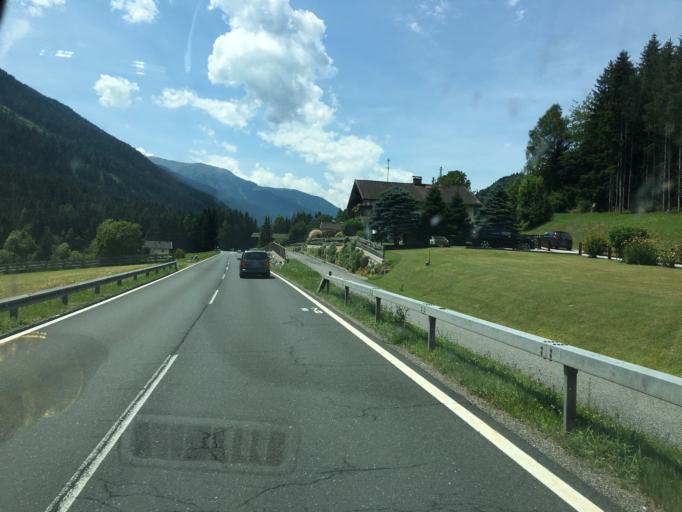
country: AT
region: Carinthia
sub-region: Politischer Bezirk Spittal an der Drau
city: Stall
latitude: 46.8817
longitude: 13.0154
